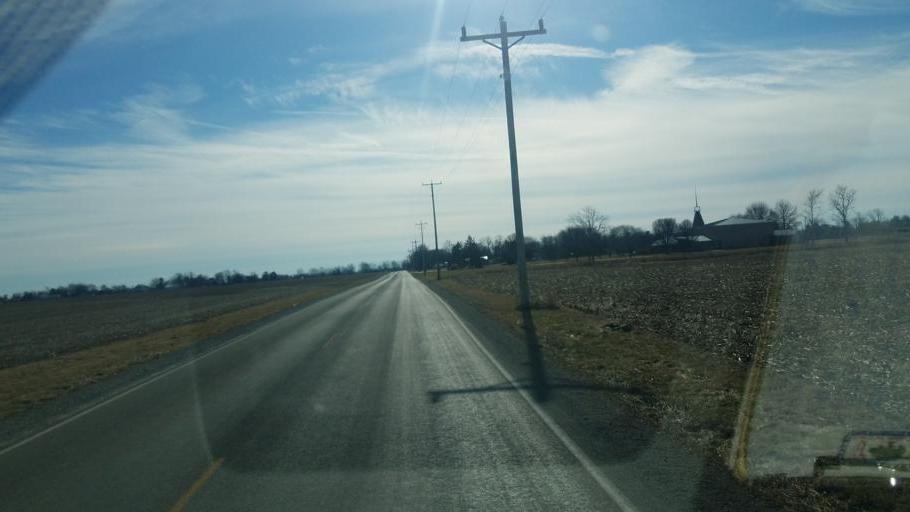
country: US
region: Ohio
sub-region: Hardin County
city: Kenton
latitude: 40.6530
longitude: -83.5762
